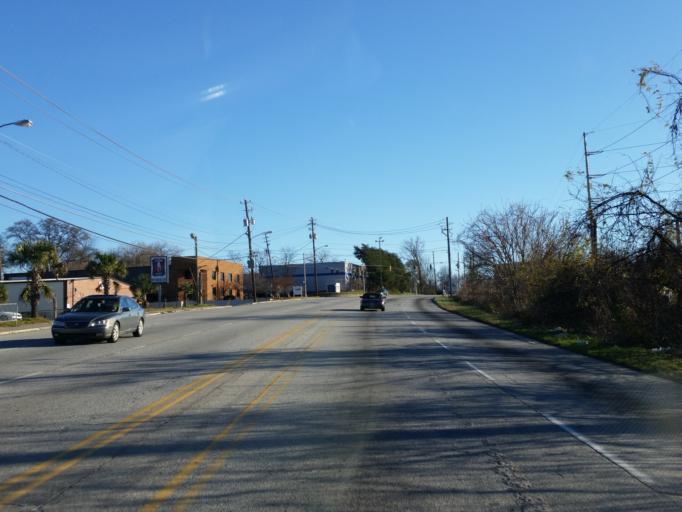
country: US
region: Georgia
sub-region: Fulton County
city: Atlanta
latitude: 33.7897
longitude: -84.4288
